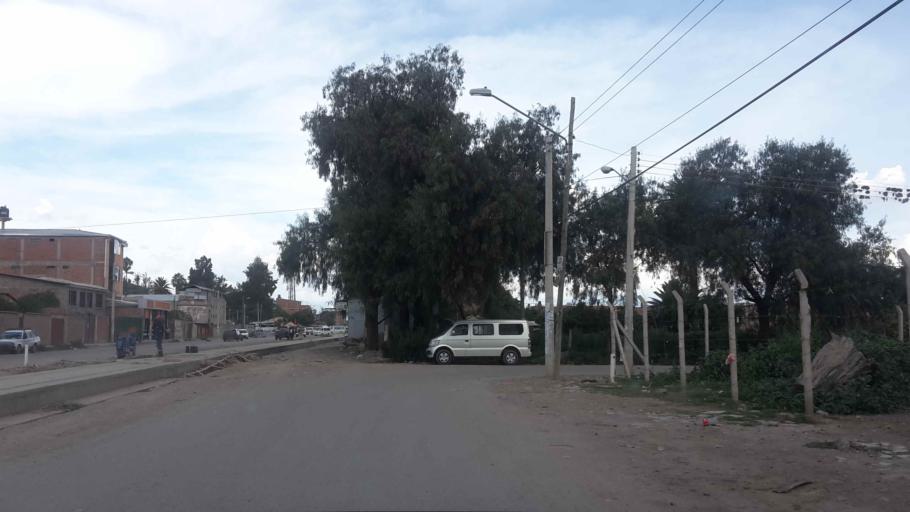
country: BO
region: Cochabamba
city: Sipe Sipe
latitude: -17.4021
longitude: -66.2845
